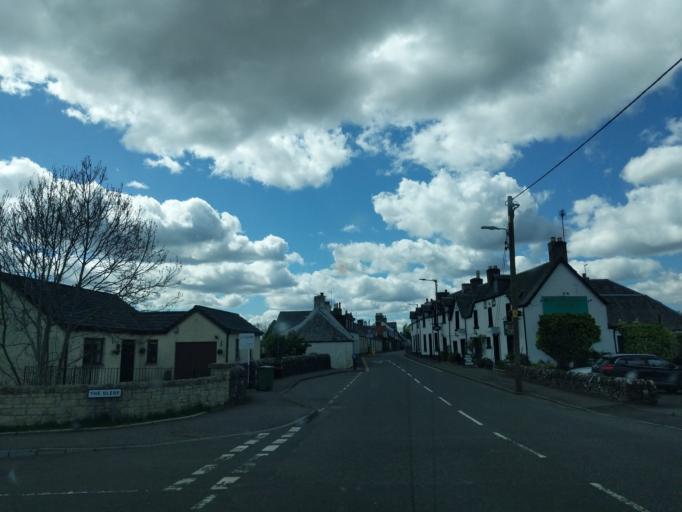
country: GB
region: Scotland
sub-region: Stirling
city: Doune
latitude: 56.1739
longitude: -4.1457
